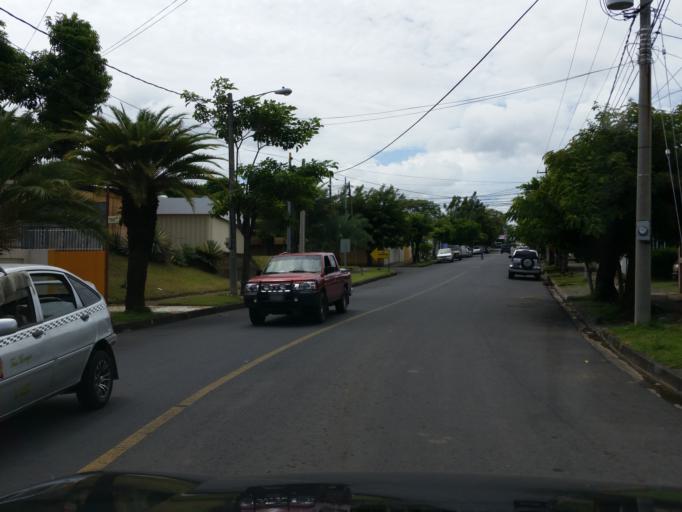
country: NI
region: Managua
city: Managua
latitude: 12.1237
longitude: -86.2581
